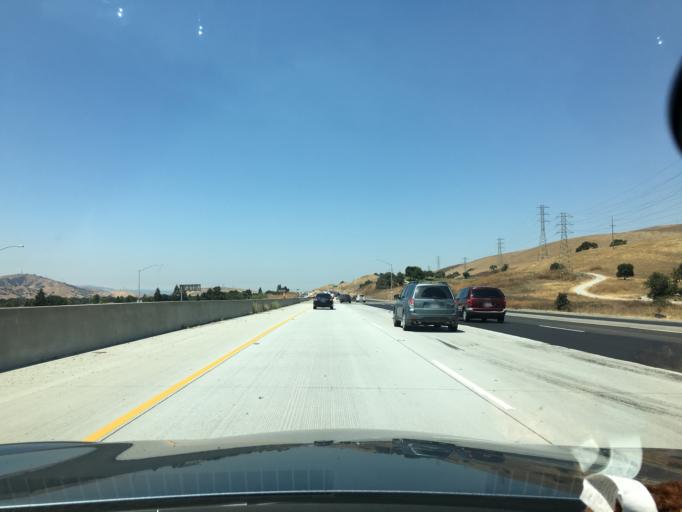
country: US
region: California
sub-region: Santa Clara County
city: Morgan Hill
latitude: 37.1926
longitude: -121.6957
